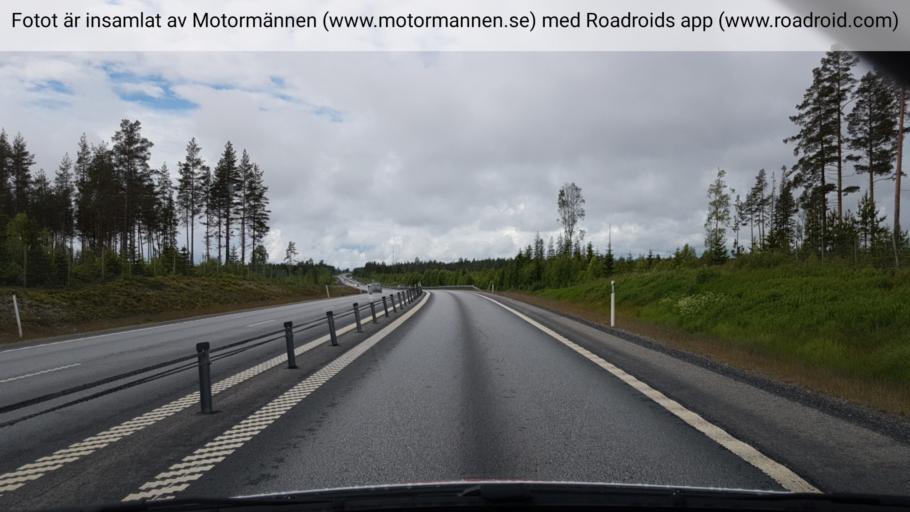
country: SE
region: Vaesterbotten
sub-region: Umea Kommun
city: Hoernefors
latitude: 63.6669
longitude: 19.9695
